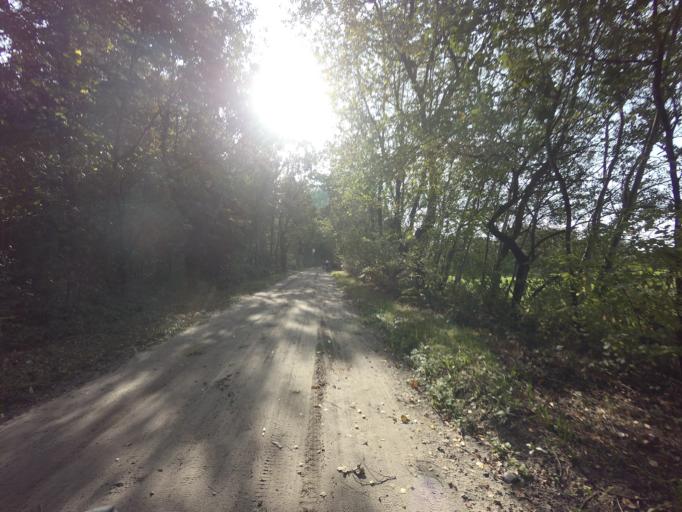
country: NL
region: North Brabant
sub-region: Gemeente Breda
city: Hoge Vucht
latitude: 51.6402
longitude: 4.8078
